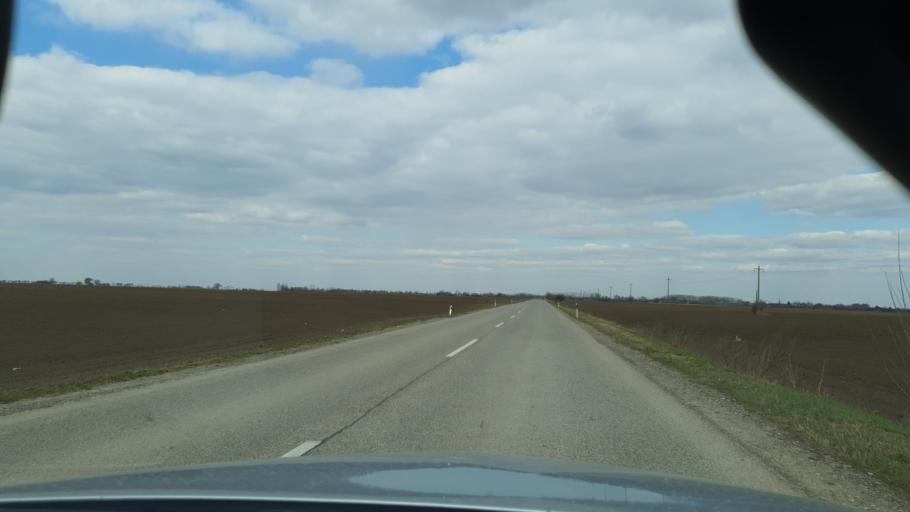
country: RS
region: Autonomna Pokrajina Vojvodina
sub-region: Juznobacki Okrug
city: Bac
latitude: 45.4353
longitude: 19.3123
